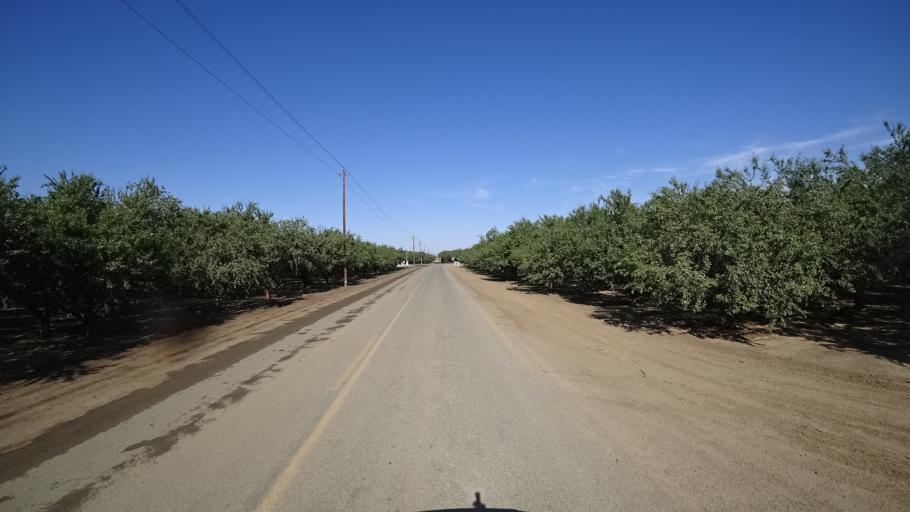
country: US
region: California
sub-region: Fresno County
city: Huron
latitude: 36.1088
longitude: -120.0465
